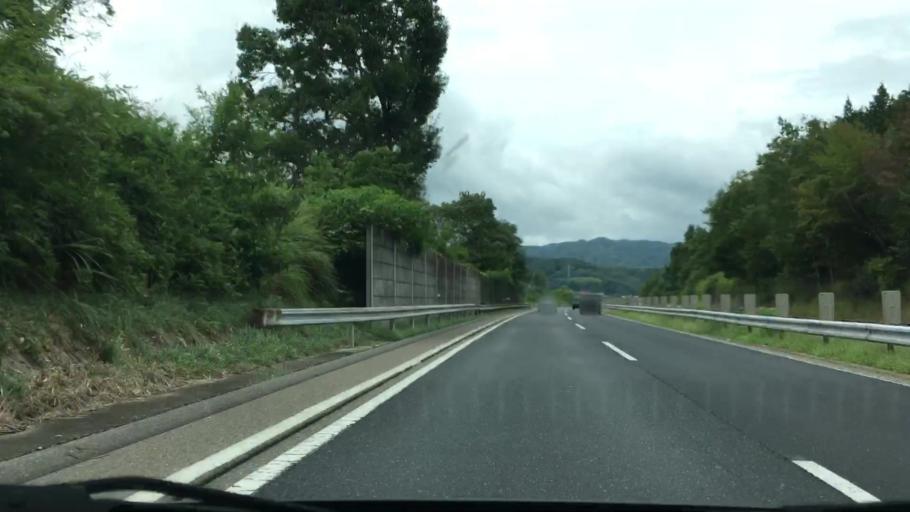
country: JP
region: Okayama
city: Tsuyama
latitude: 35.0579
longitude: 133.9264
